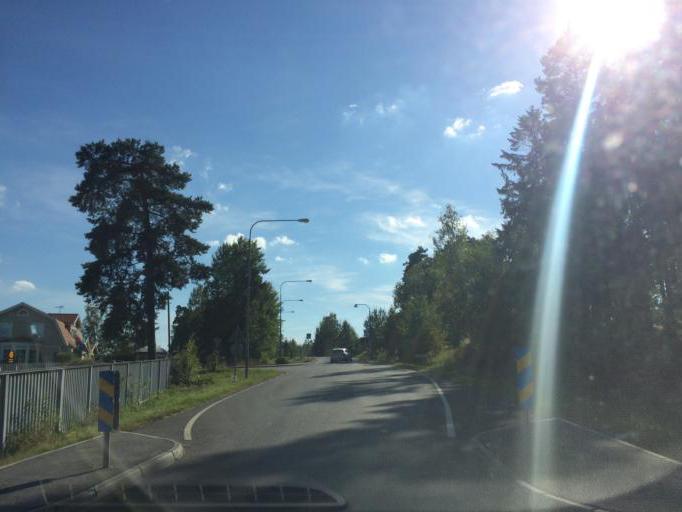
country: SE
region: Stockholm
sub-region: Upplands Vasby Kommun
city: Upplands Vaesby
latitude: 59.5041
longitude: 17.9501
